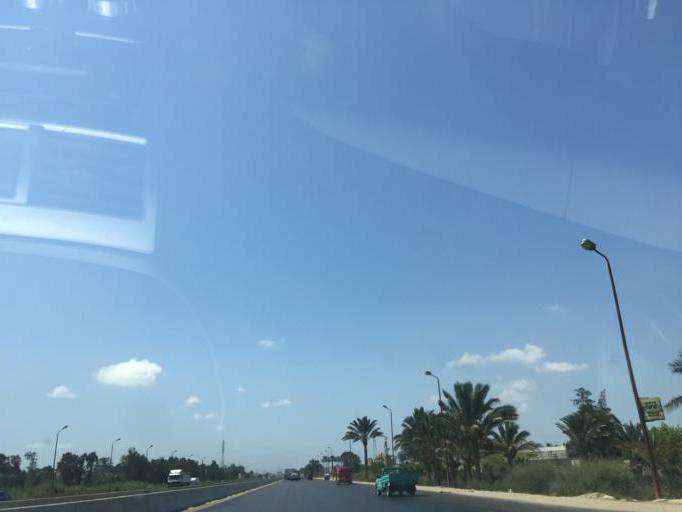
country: EG
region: Alexandria
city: Alexandria
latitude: 30.9873
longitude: 29.8131
